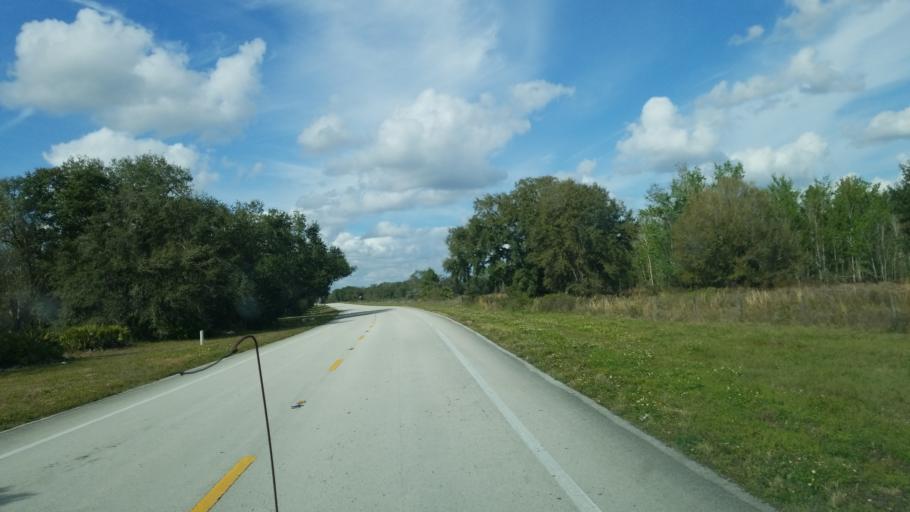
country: US
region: Florida
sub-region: Brevard County
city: June Park
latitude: 27.9534
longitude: -81.0006
